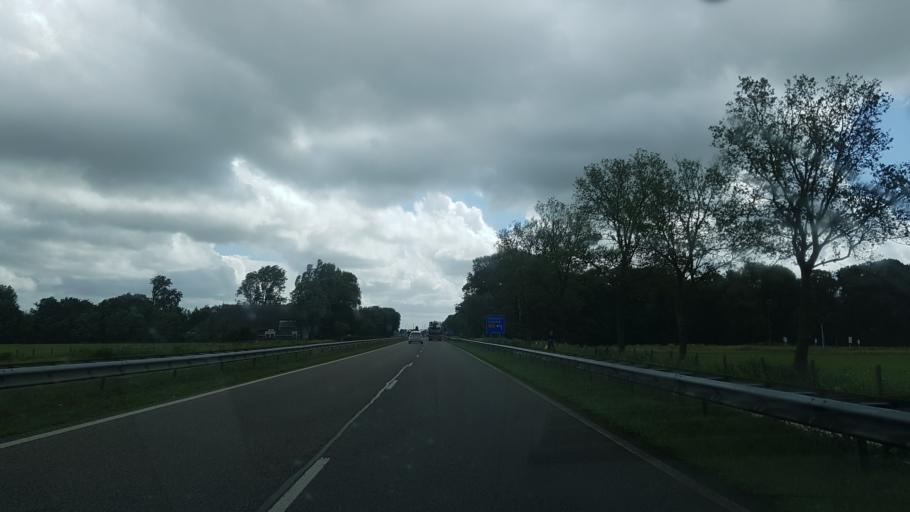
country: NL
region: Friesland
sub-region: Gemeente Tytsjerksteradiel
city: Tytsjerk
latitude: 53.2178
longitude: 5.9000
